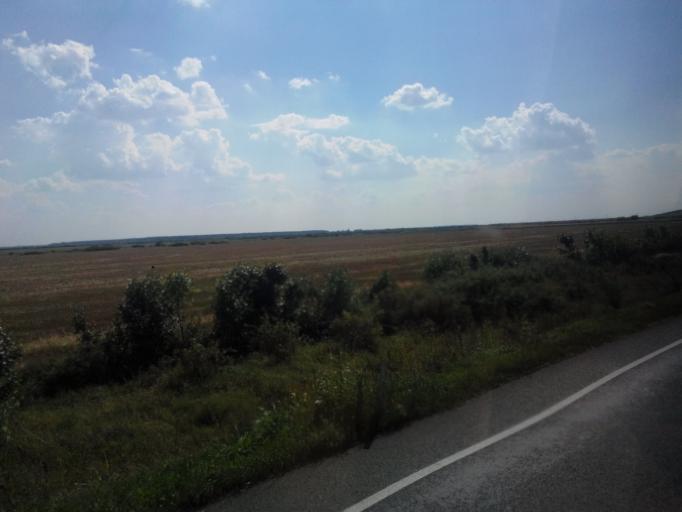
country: RO
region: Timis
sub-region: Oras Recas
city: Recas
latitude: 45.7932
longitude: 21.5582
